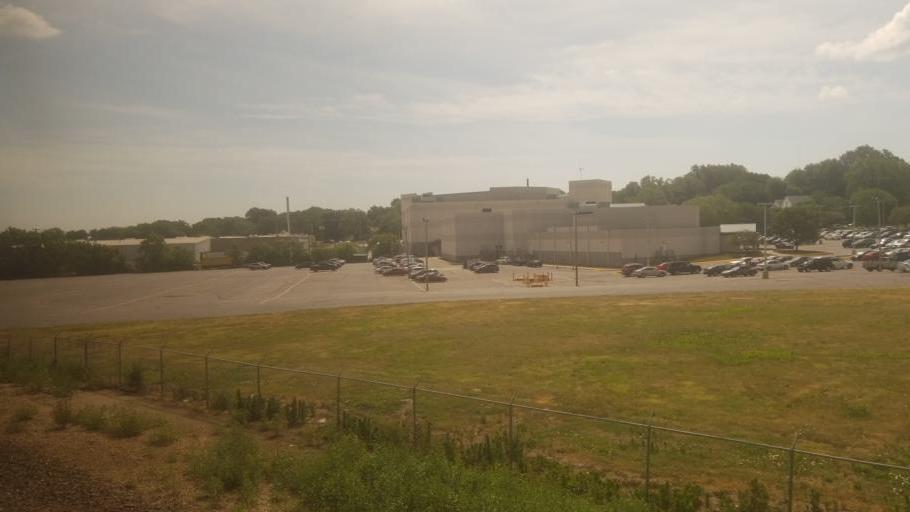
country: US
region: Missouri
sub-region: Clay County
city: North Kansas City
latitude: 39.1026
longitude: -94.5168
